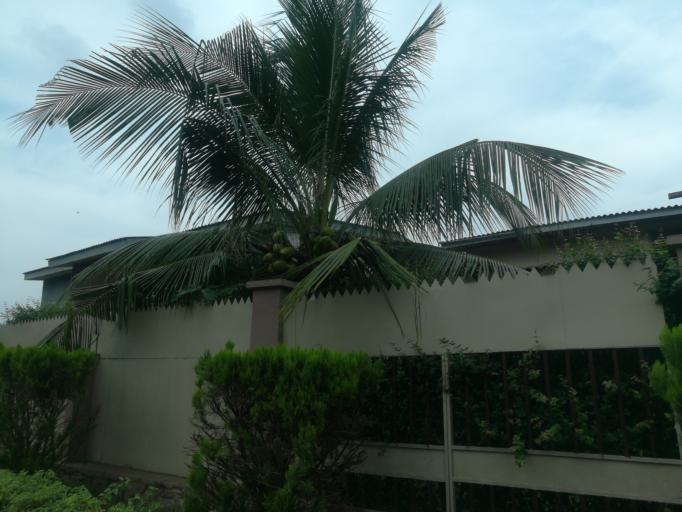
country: NG
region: Oyo
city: Ibadan
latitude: 7.4132
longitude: 3.8996
